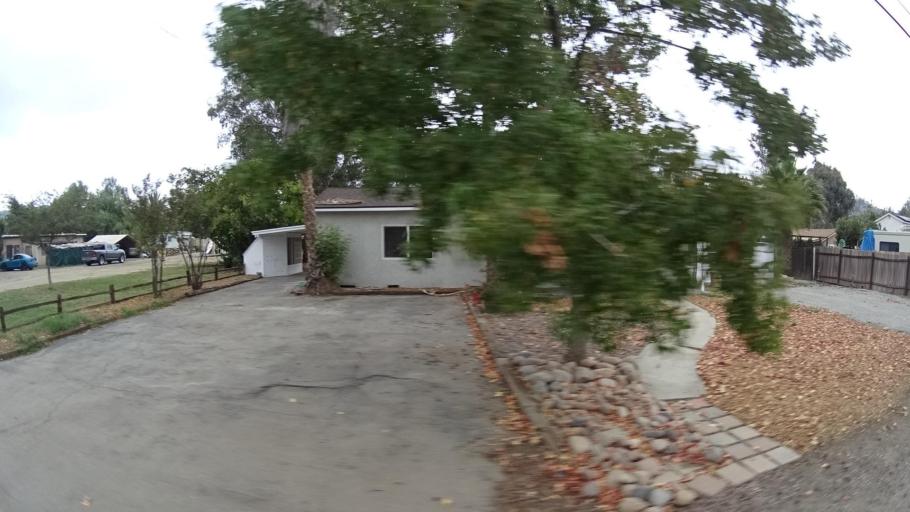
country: US
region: California
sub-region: San Diego County
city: Eucalyptus Hills
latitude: 32.8671
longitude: -116.9404
